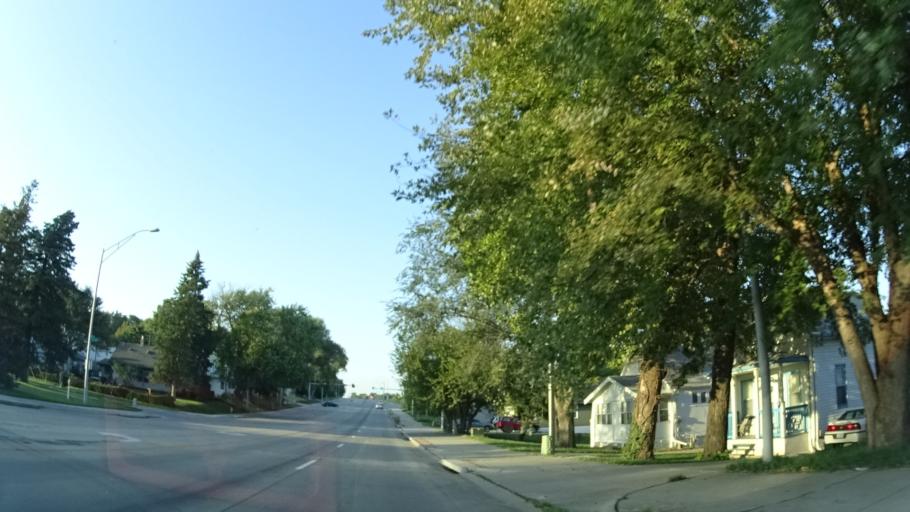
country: US
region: Nebraska
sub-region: Douglas County
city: Omaha
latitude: 41.2080
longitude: -95.9335
